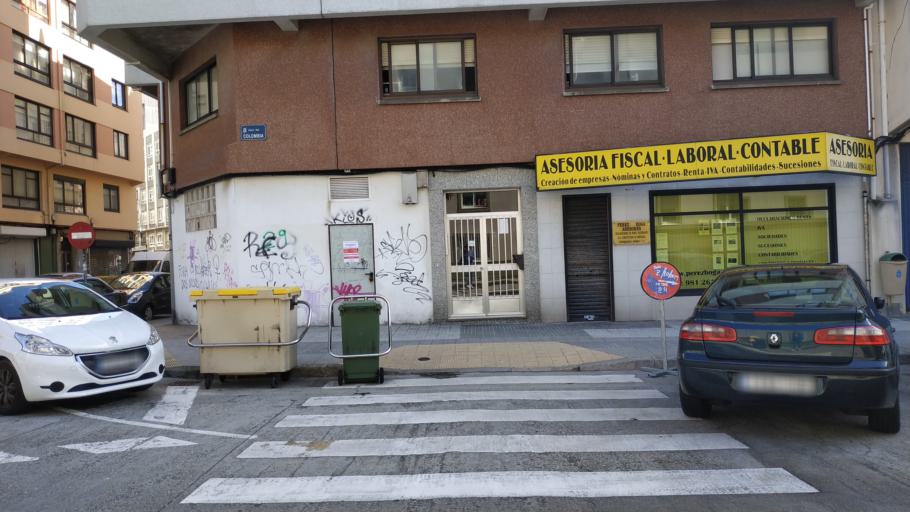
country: ES
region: Galicia
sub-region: Provincia da Coruna
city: A Coruna
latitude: 43.3713
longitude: -8.4239
